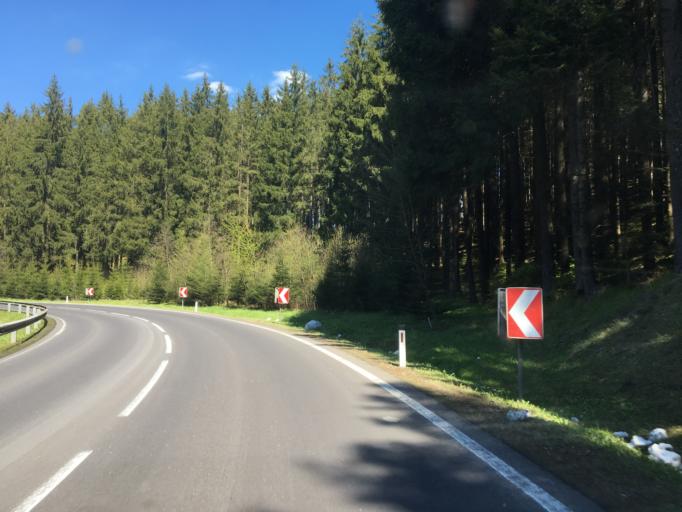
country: AT
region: Upper Austria
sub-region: Politischer Bezirk Urfahr-Umgebung
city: Bad Leonfelden
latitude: 48.4898
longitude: 14.2975
